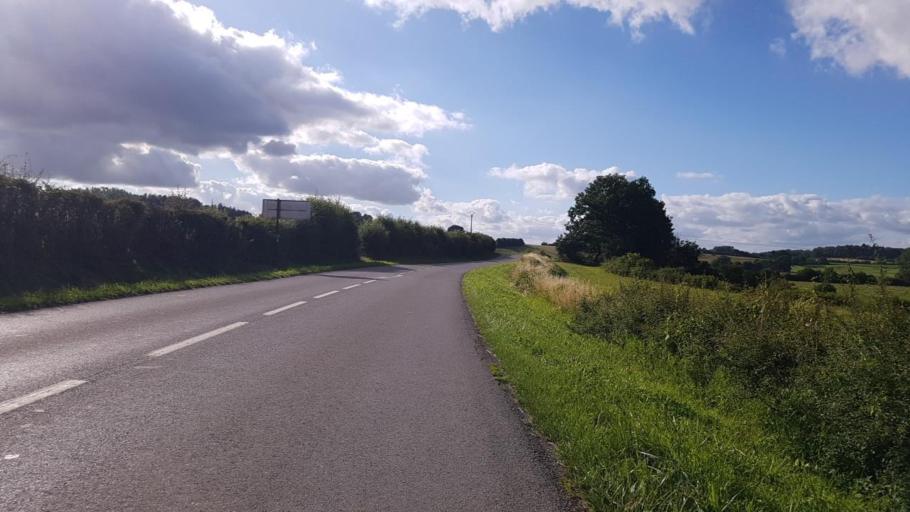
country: FR
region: Picardie
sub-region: Departement de l'Aisne
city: Hirson
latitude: 49.9210
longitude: 4.0558
